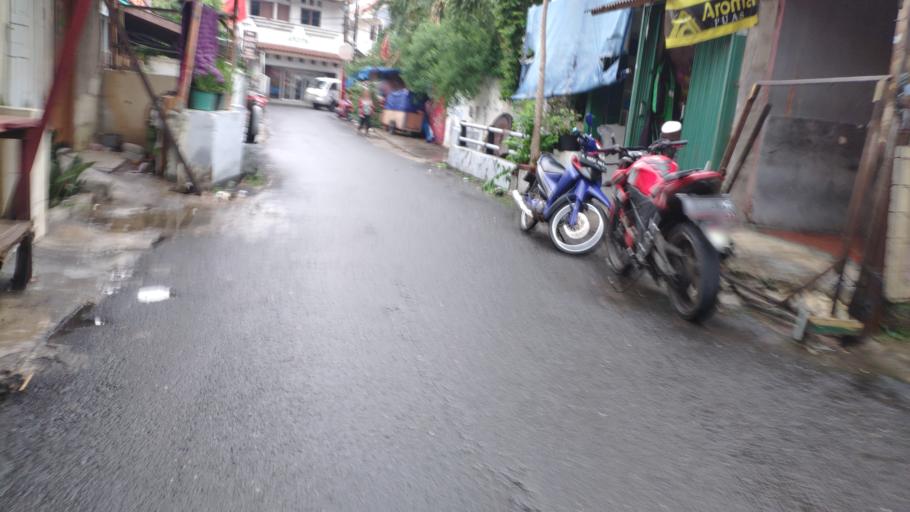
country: ID
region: Jakarta Raya
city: Jakarta
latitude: -6.2068
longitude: 106.8711
